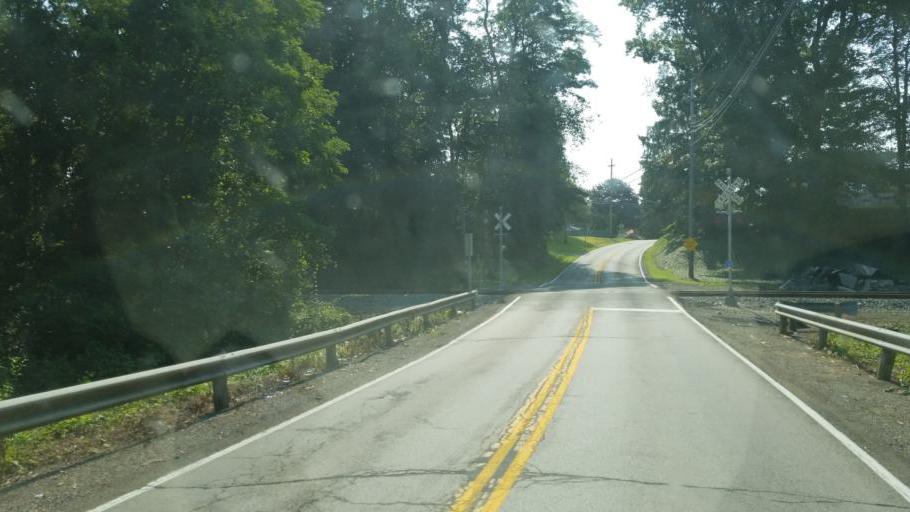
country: US
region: Ohio
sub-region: Lake County
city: Painesville
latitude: 41.7411
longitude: -81.2078
